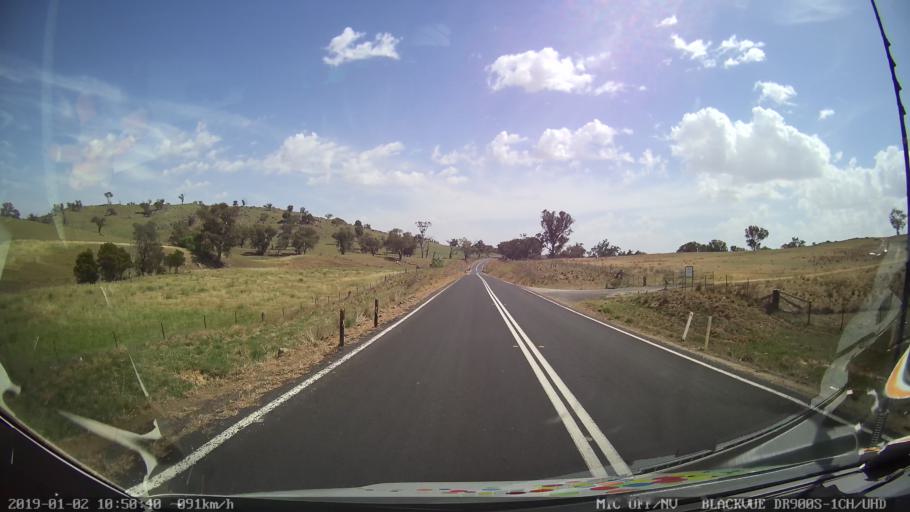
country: AU
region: New South Wales
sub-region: Cootamundra
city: Cootamundra
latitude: -34.7115
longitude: 148.2757
